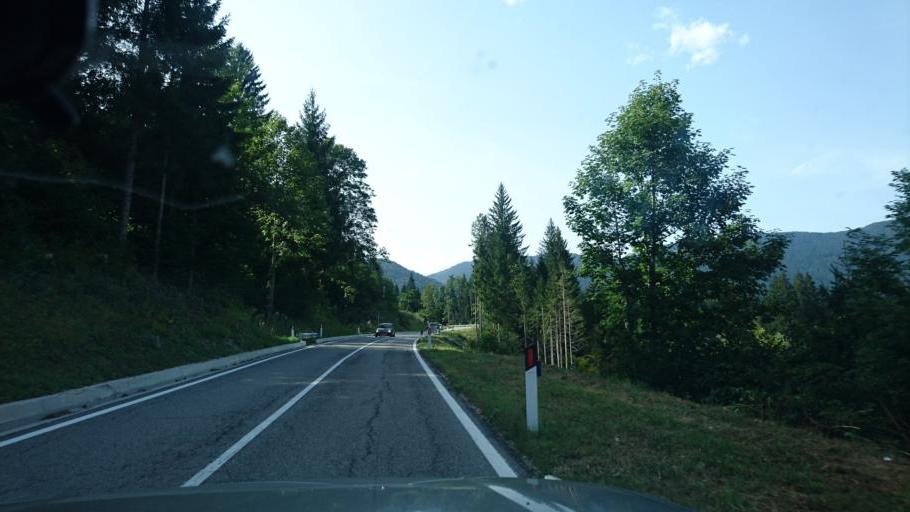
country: IT
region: Friuli Venezia Giulia
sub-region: Provincia di Udine
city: Tarvisio
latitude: 46.5032
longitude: 13.6237
